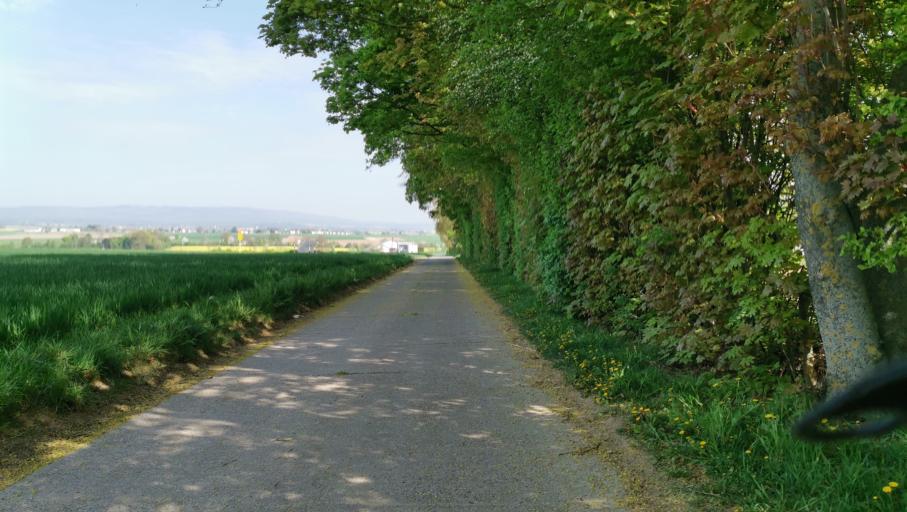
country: DE
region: Hesse
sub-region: Regierungsbezirk Darmstadt
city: Karben
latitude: 50.2219
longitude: 8.7305
